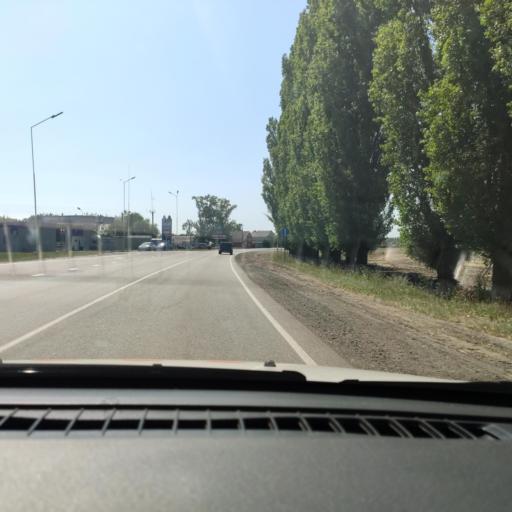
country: RU
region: Voronezj
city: Imeni Pervogo Maya
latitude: 50.7160
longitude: 39.4096
